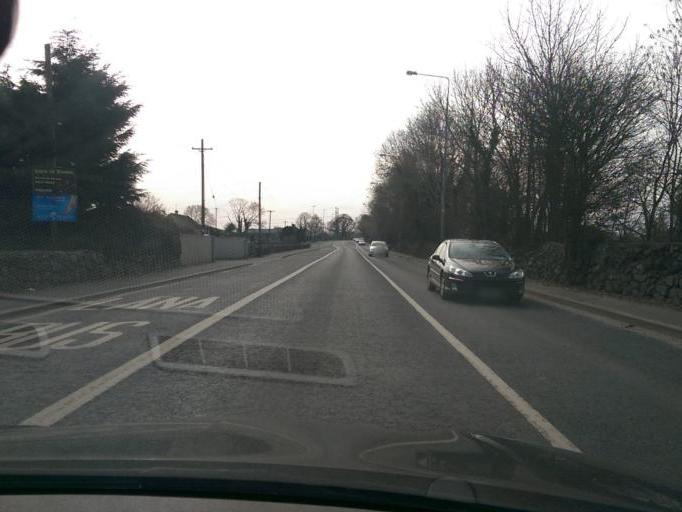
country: IE
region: Connaught
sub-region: County Galway
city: Claregalway
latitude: 53.3561
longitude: -8.9319
